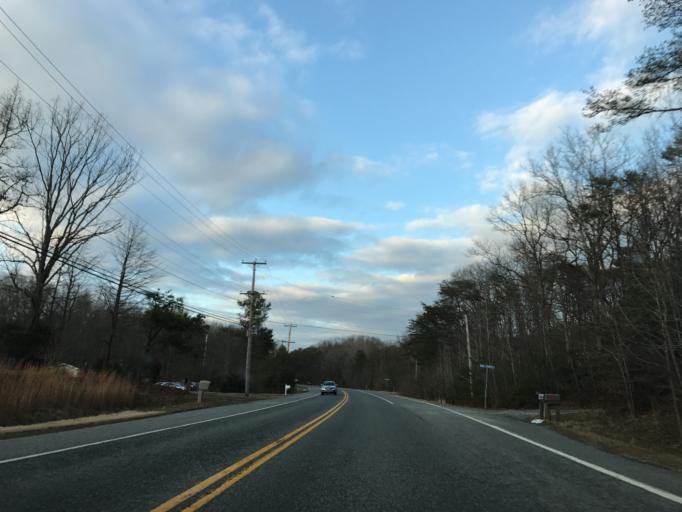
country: US
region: Maryland
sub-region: Cecil County
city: Charlestown
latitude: 39.5424
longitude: -75.9490
